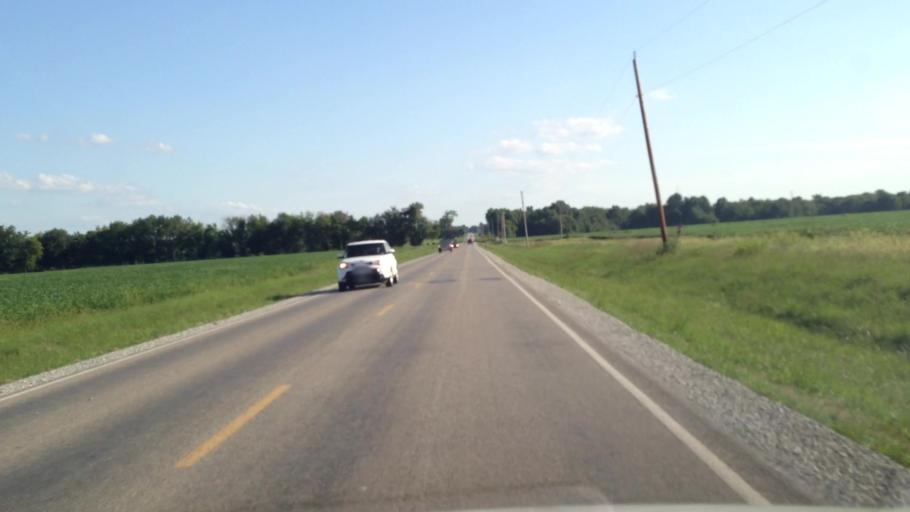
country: US
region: Kansas
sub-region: Crawford County
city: Pittsburg
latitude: 37.3555
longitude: -94.6315
